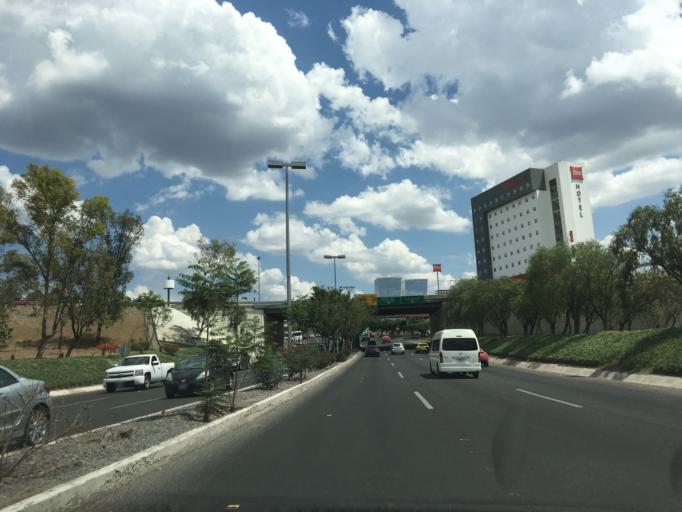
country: MX
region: Queretaro
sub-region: Queretaro
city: Santiago de Queretaro
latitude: 20.5809
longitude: -100.3618
